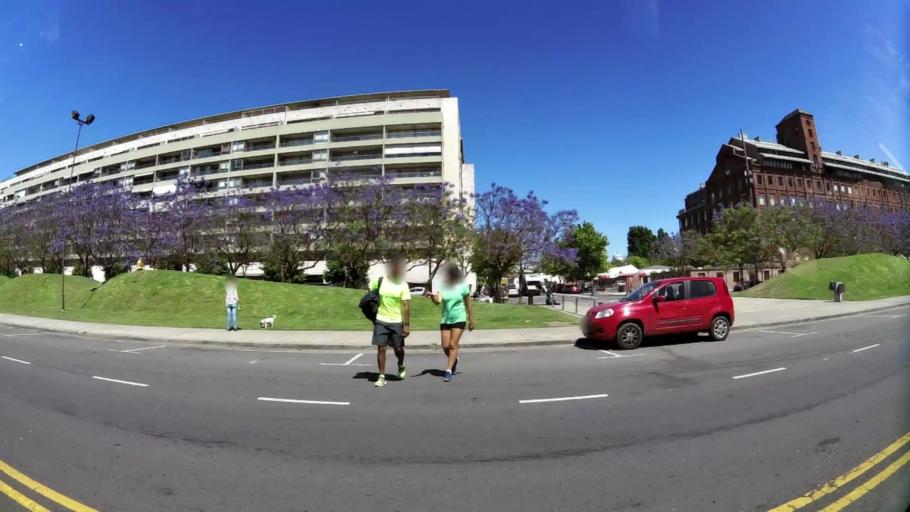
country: AR
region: Buenos Aires F.D.
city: Buenos Aires
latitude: -34.6148
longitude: -58.3606
